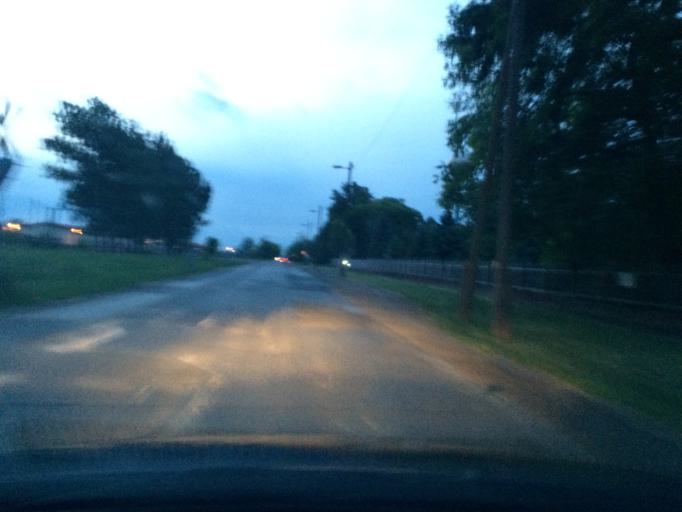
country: HU
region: Hajdu-Bihar
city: Hajdunanas
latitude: 47.9051
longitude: 21.4043
